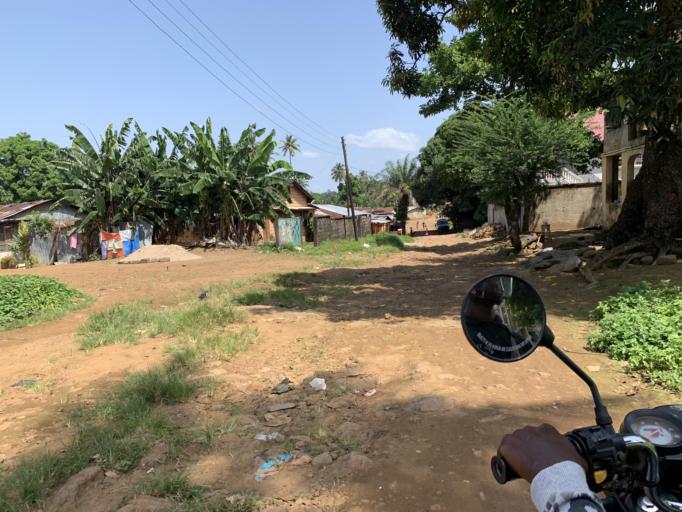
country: SL
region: Western Area
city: Hastings
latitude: 8.3830
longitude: -13.1382
